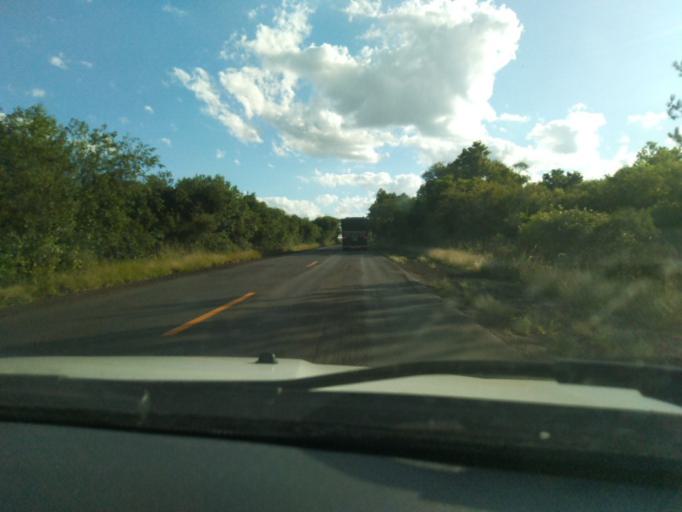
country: AR
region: Corrientes
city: Garruchos
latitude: -28.5433
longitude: -55.5529
